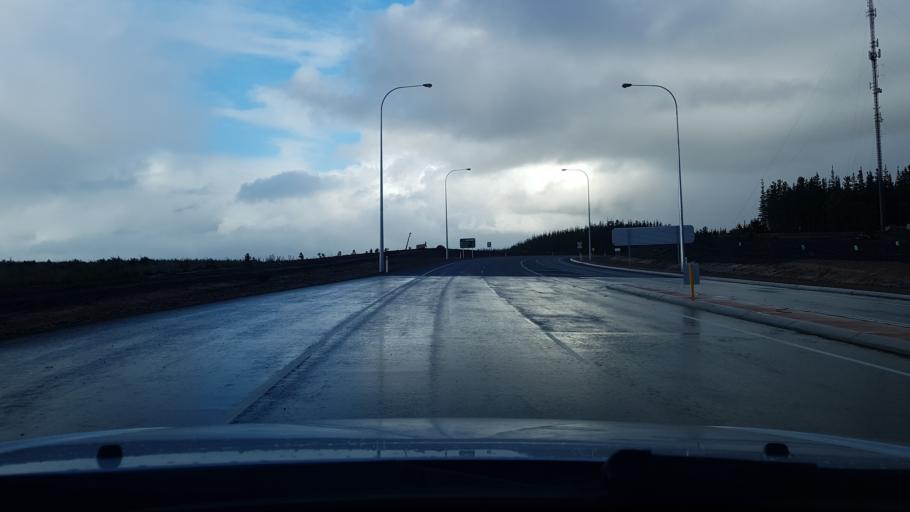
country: AU
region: Western Australia
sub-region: Augusta-Margaret River Shire
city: Margaret River
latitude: -33.9331
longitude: 115.0841
